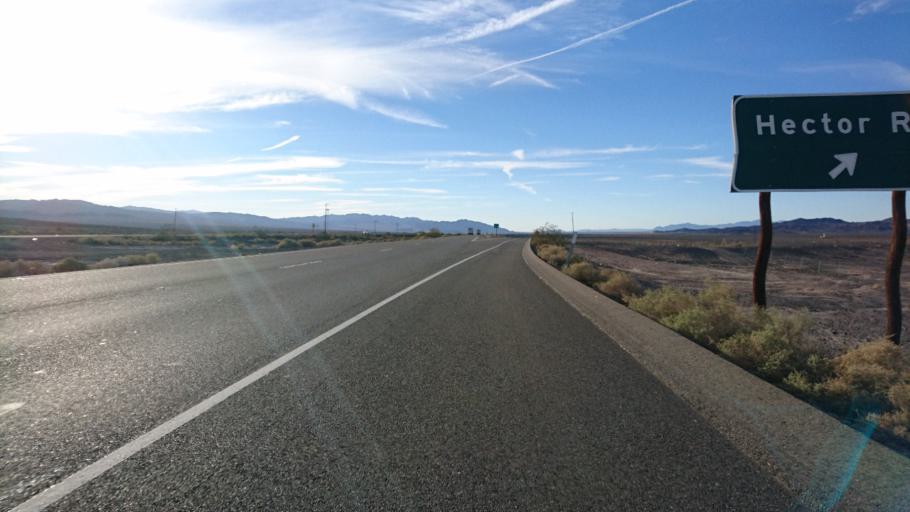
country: US
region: California
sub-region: San Bernardino County
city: Fort Irwin
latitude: 34.7878
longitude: -116.4484
